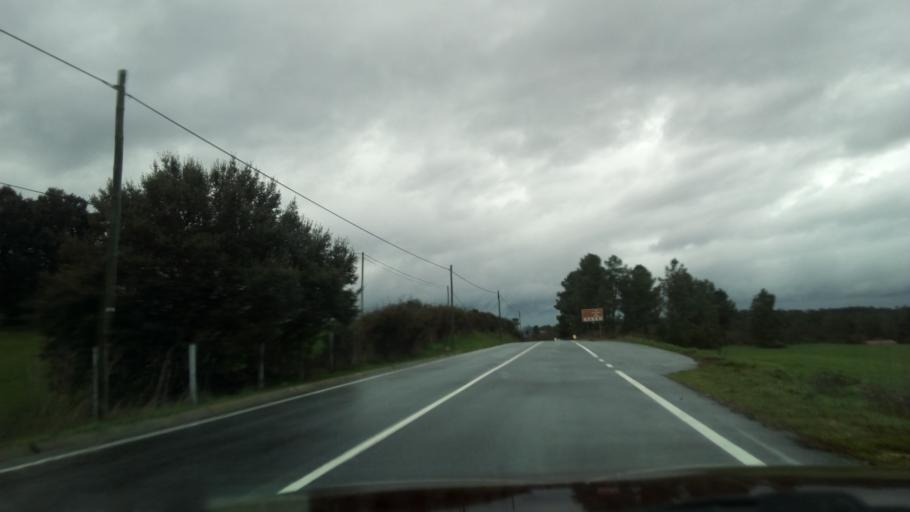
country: PT
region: Guarda
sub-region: Celorico da Beira
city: Celorico da Beira
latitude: 40.6225
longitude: -7.3182
